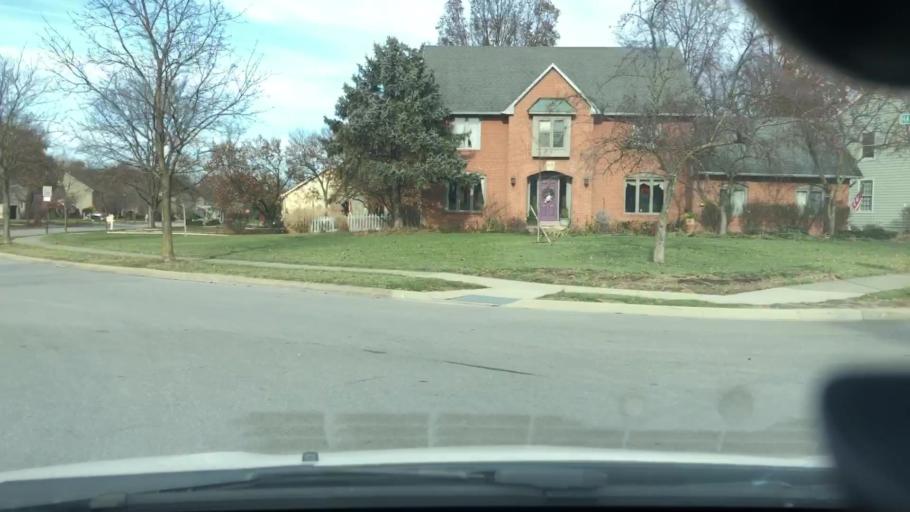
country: US
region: Ohio
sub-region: Franklin County
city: Westerville
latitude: 40.1359
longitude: -82.8917
